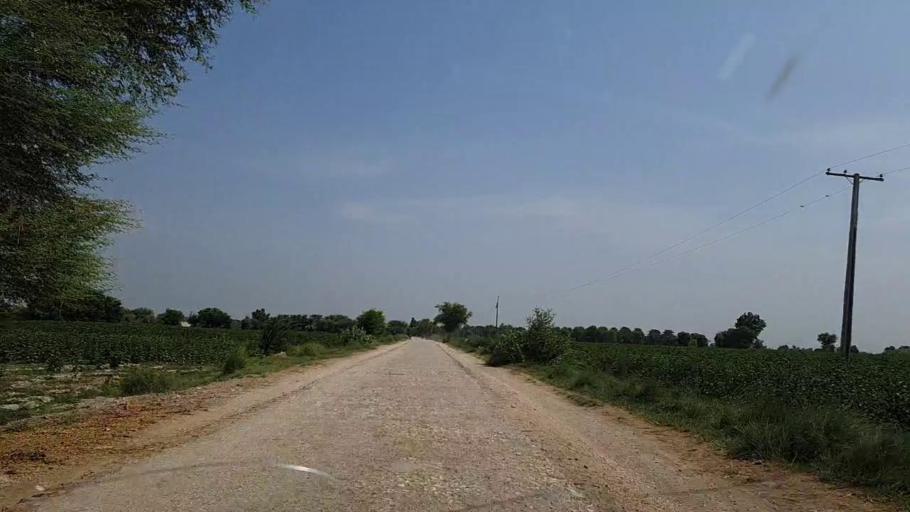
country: PK
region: Sindh
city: Khanpur
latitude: 27.7890
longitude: 69.3181
